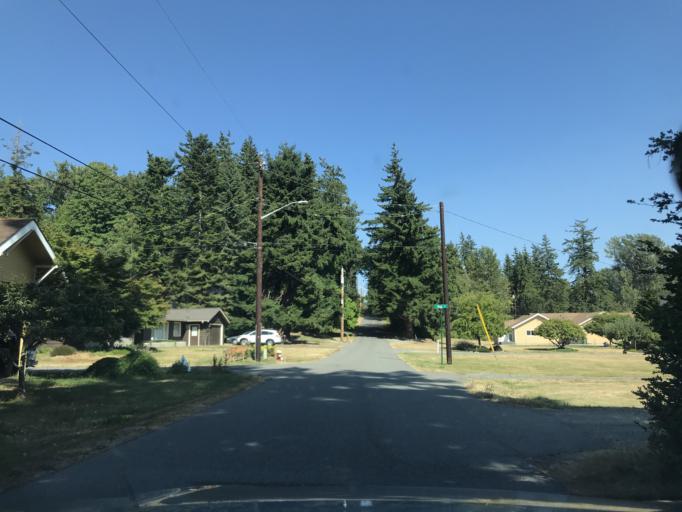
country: US
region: Washington
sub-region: Whatcom County
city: Bellingham
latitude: 48.7807
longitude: -122.4837
